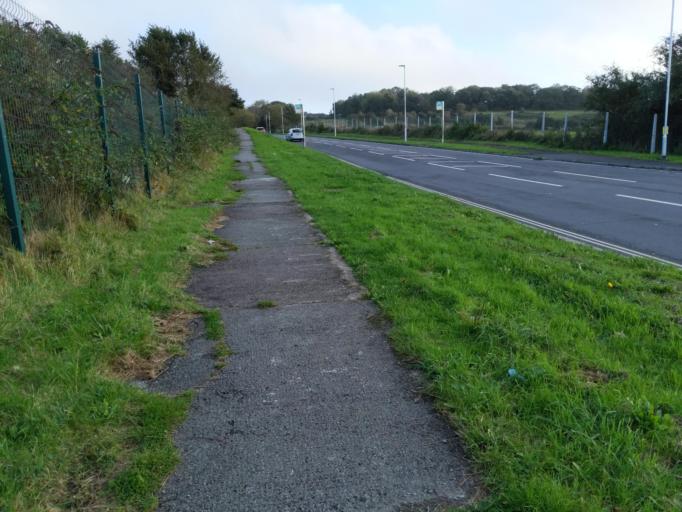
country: GB
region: England
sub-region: Cornwall
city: Saltash
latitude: 50.4163
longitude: -4.1864
